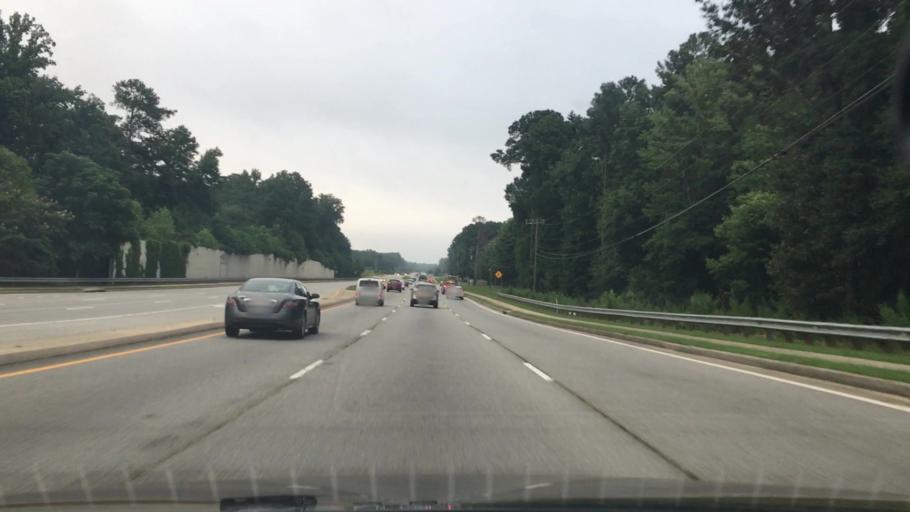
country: US
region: Georgia
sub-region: Fayette County
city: Peachtree City
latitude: 33.3793
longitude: -84.5758
